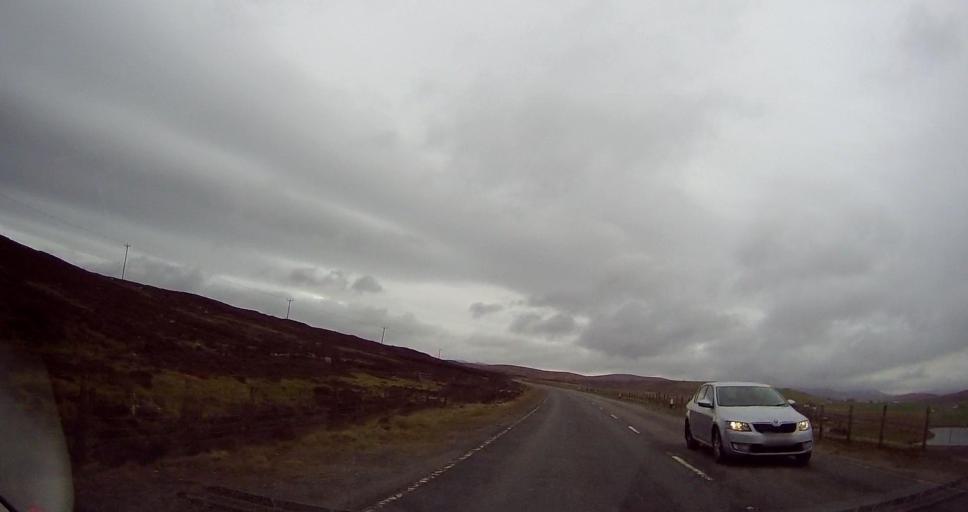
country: GB
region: Scotland
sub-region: Shetland Islands
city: Lerwick
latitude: 60.2247
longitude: -1.2348
